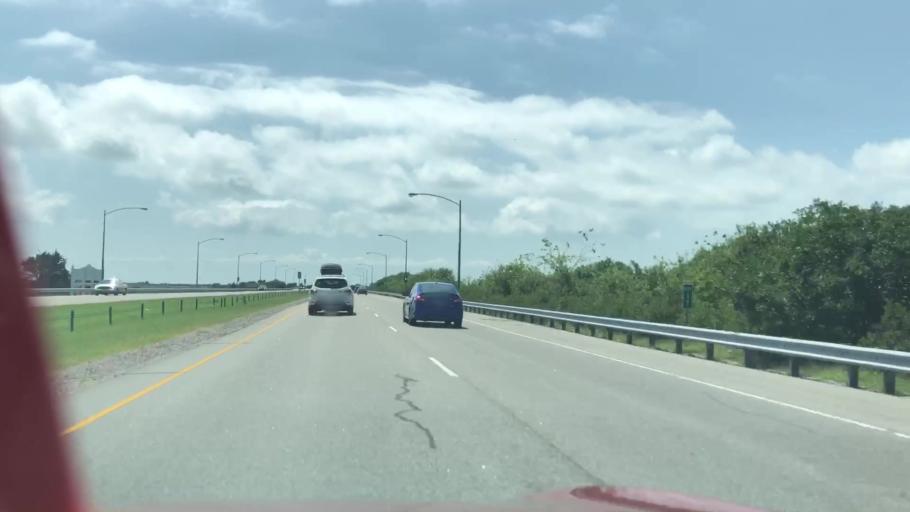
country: US
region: Virginia
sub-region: Northampton County
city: Cape Charles
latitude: 37.1027
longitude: -75.9693
